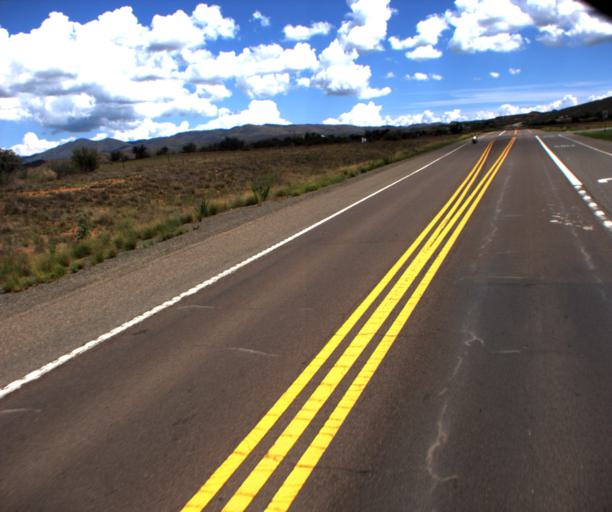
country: US
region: Arizona
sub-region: Yavapai County
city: Dewey-Humboldt
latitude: 34.5308
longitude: -112.2216
